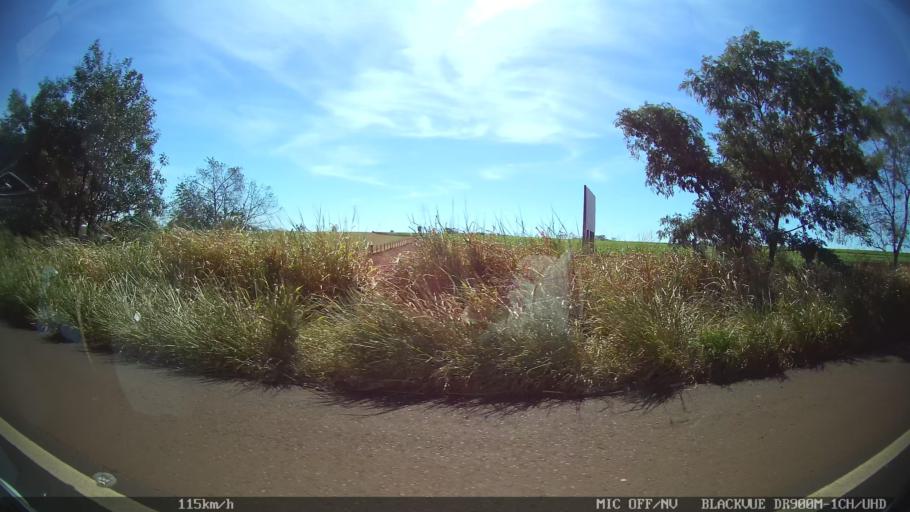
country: BR
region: Sao Paulo
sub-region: Franca
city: Franca
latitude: -20.5616
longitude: -47.6159
